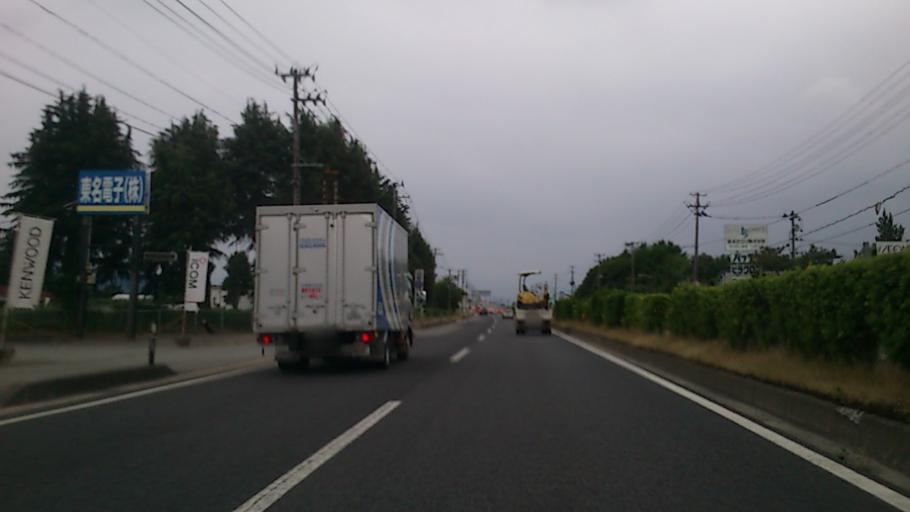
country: JP
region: Yamagata
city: Tendo
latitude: 38.3386
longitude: 140.3719
